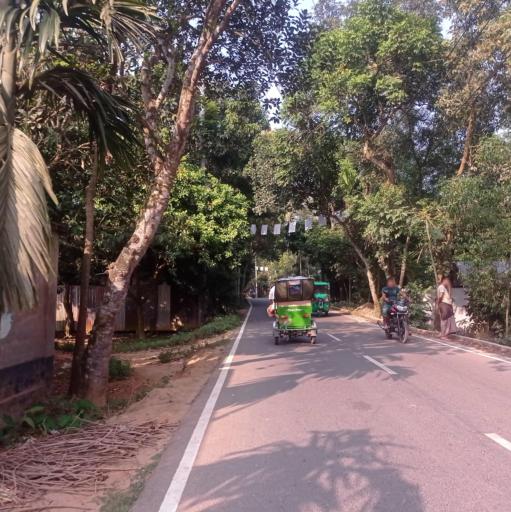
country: BD
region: Dhaka
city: Bhairab Bazar
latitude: 24.0491
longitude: 90.8355
